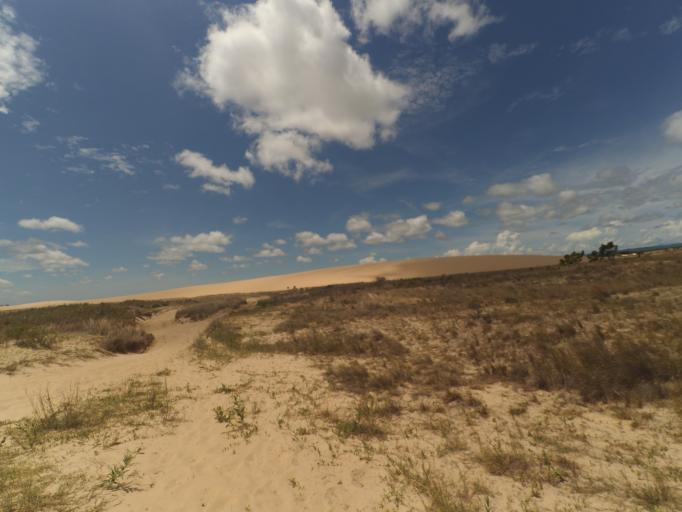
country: BO
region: Santa Cruz
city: Santa Cruz de la Sierra
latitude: -17.9379
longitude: -63.1579
